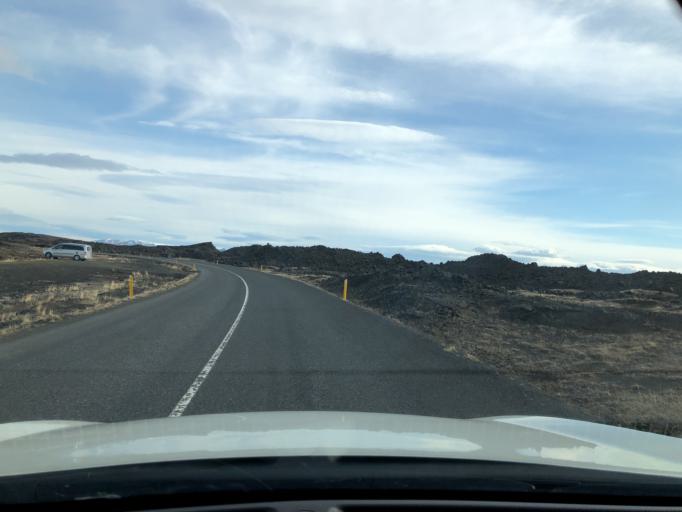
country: IS
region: Northeast
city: Laugar
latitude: 65.5631
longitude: -16.9425
